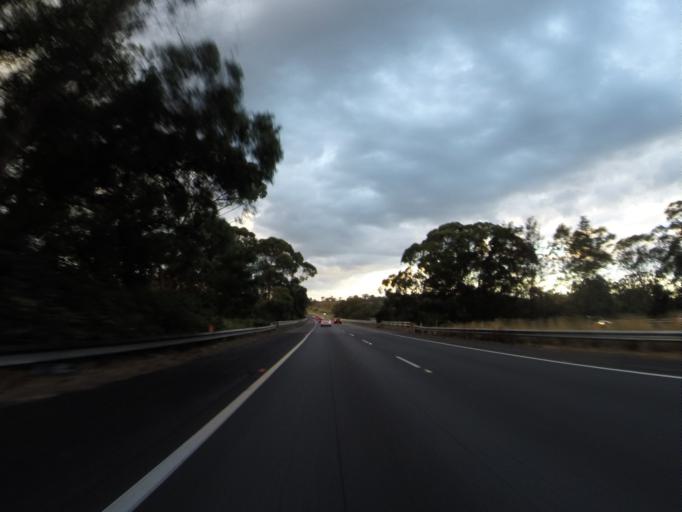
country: AU
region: New South Wales
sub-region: Campbelltown Municipality
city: Glen Alpine
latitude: -34.1205
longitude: 150.7557
